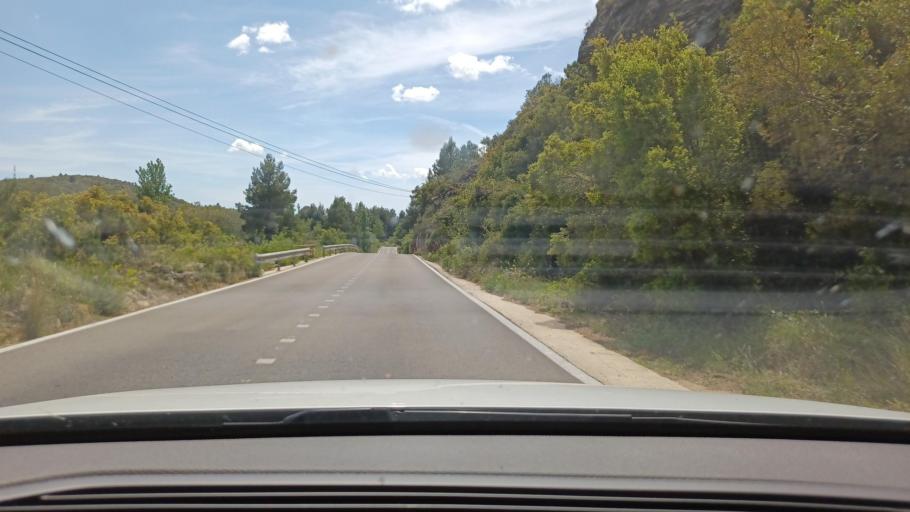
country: ES
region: Valencia
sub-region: Provincia de Castello
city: Rosell
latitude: 40.6583
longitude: 0.2671
